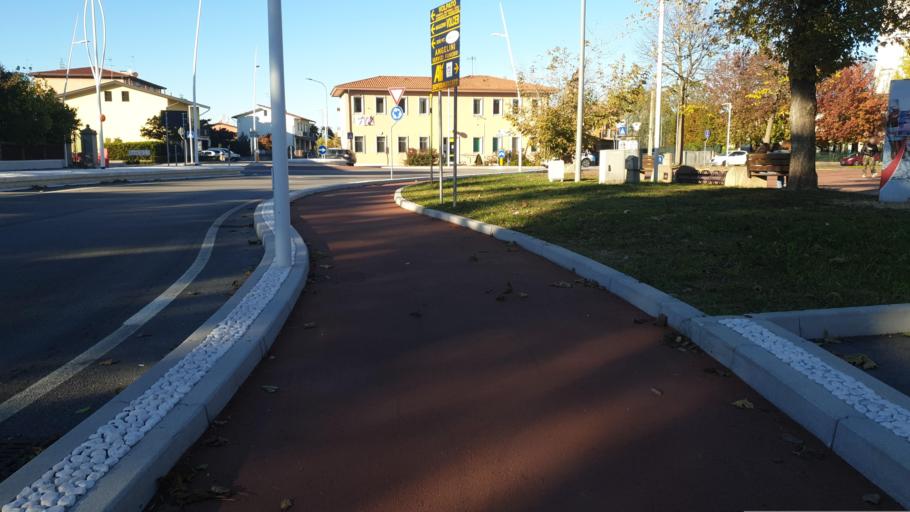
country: IT
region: Veneto
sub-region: Provincia di Venezia
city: Cazzago-Ex Polo
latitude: 45.4398
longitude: 12.0742
